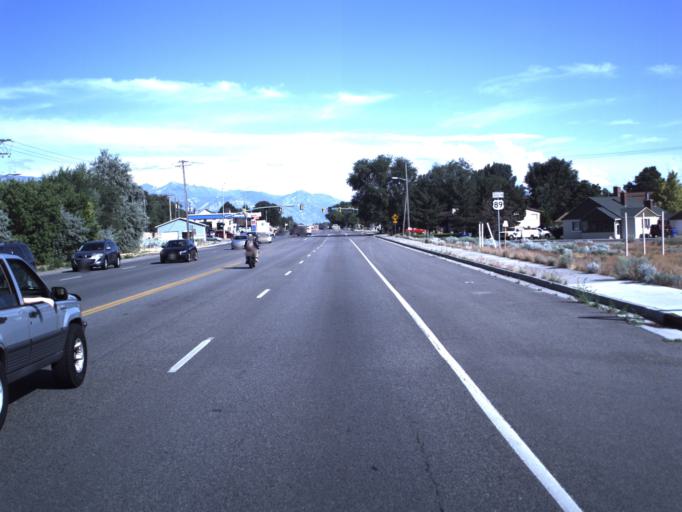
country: US
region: Utah
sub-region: Utah County
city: Lehi
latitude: 40.4031
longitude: -111.8564
